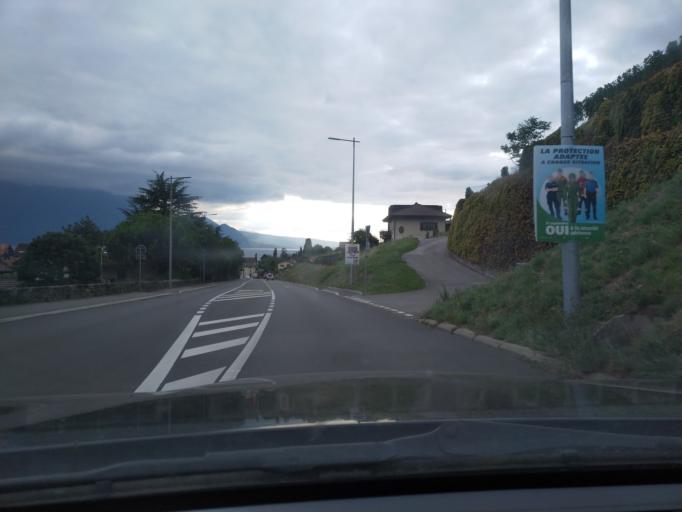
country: CH
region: Vaud
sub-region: Riviera-Pays-d'Enhaut District
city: Jongny
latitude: 46.4730
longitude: 6.8441
